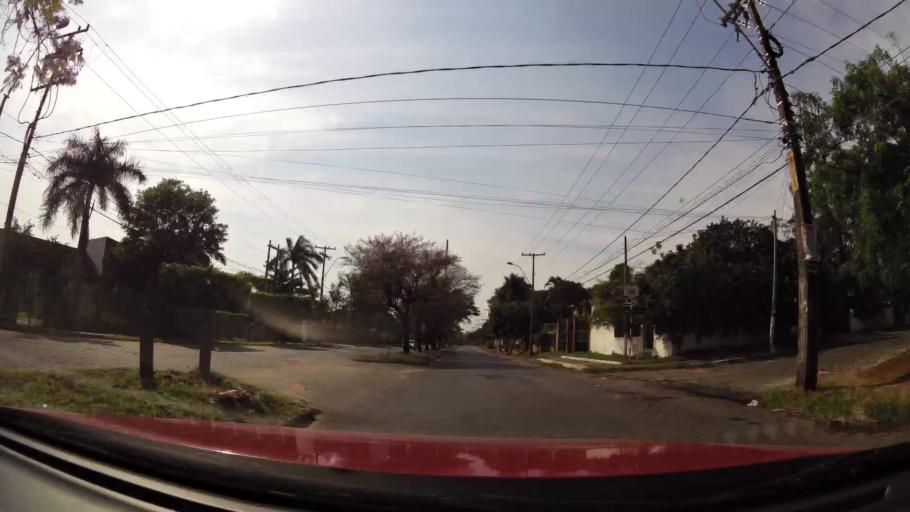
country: PY
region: Central
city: Fernando de la Mora
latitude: -25.2654
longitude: -57.5545
